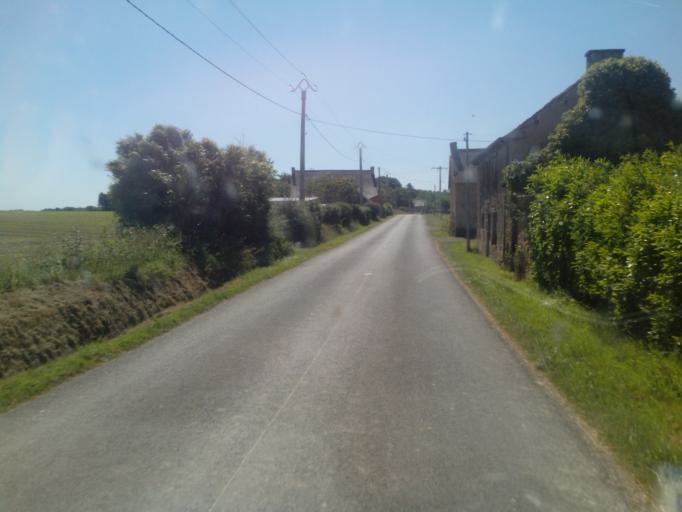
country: FR
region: Brittany
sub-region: Departement du Morbihan
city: Mauron
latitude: 48.1466
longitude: -2.3351
